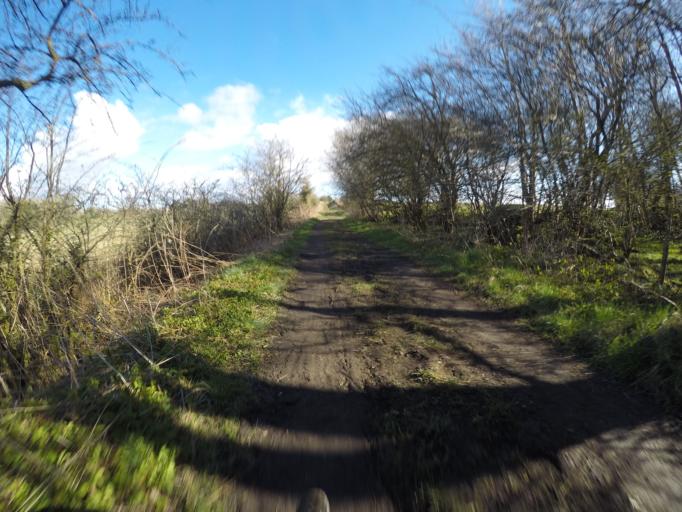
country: GB
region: Scotland
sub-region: North Ayrshire
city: Irvine
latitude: 55.6492
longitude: -4.6590
